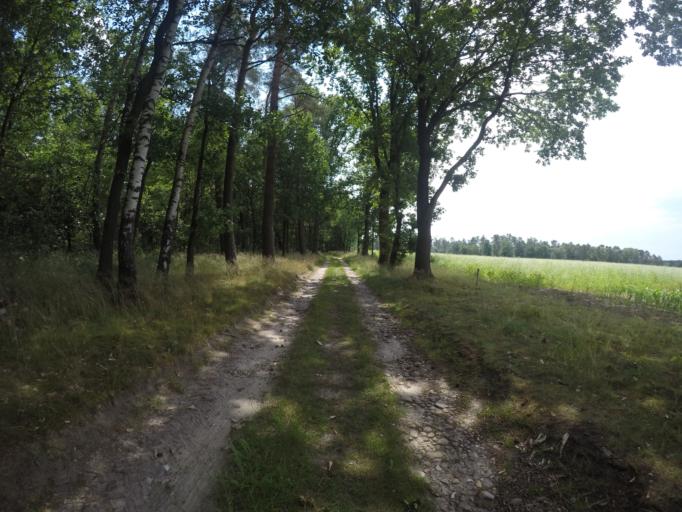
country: DE
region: Lower Saxony
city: Jesteburg
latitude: 53.2706
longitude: 9.9277
